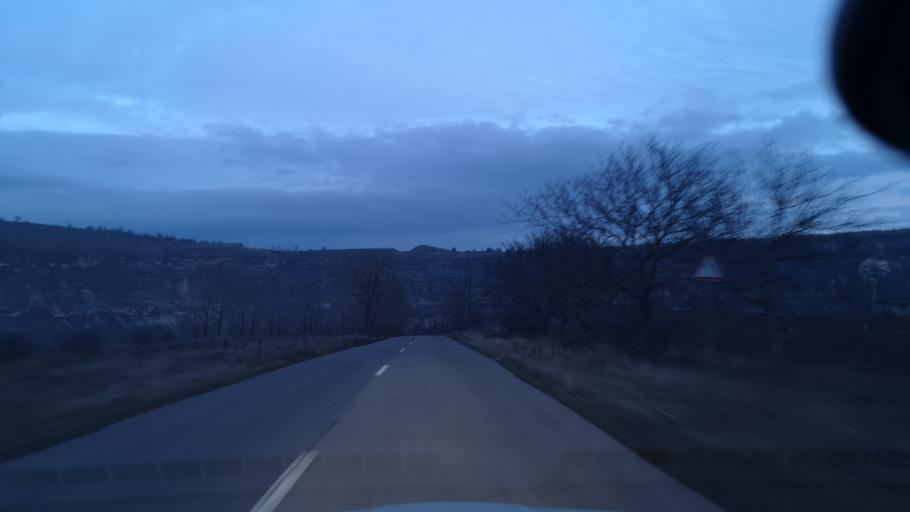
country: MD
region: Telenesti
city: Cocieri
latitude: 47.3074
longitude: 28.9835
